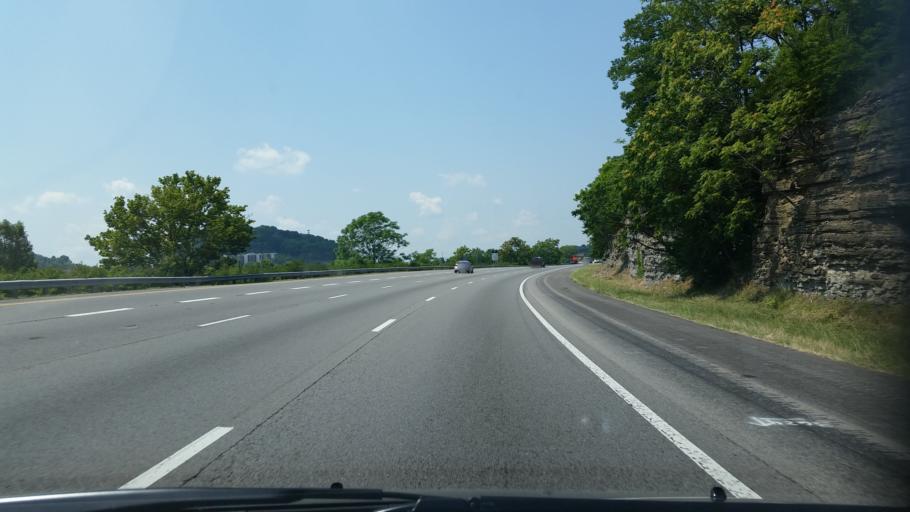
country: US
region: Tennessee
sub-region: Williamson County
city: Brentwood
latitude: 36.0475
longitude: -86.7768
